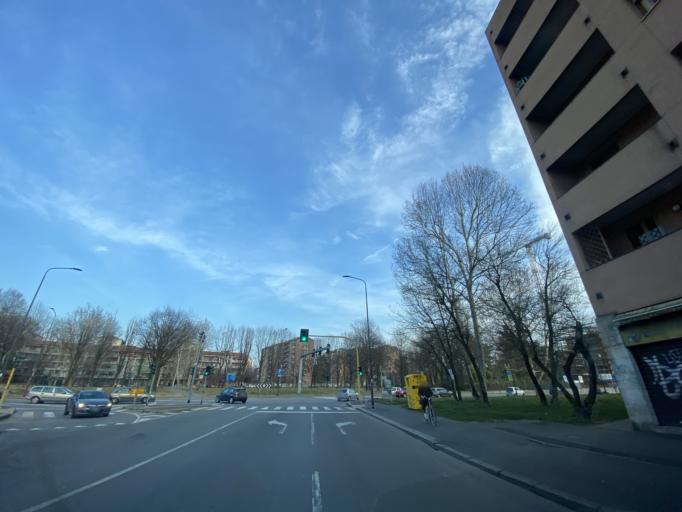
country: IT
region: Lombardy
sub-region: Citta metropolitana di Milano
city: Cormano
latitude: 45.5239
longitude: 9.1657
